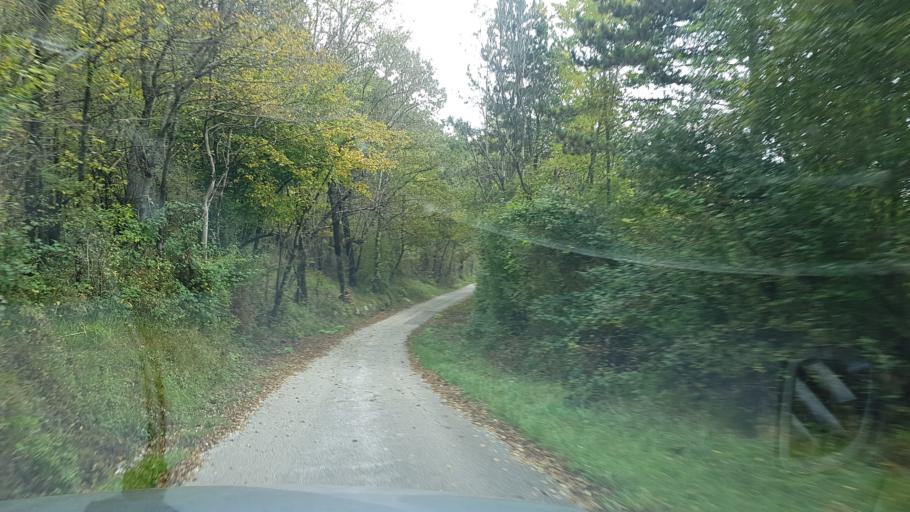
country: HR
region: Istarska
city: Buzet
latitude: 45.4341
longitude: 14.0603
